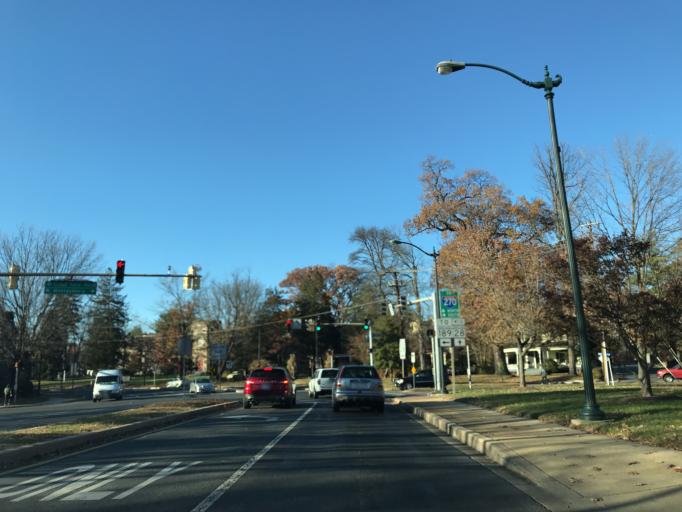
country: US
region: Maryland
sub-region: Montgomery County
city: Rockville
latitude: 39.0835
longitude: -77.1565
